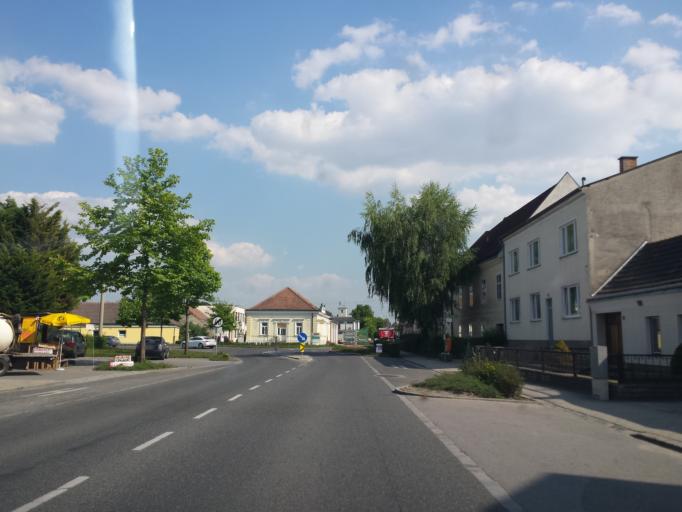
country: AT
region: Lower Austria
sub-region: Politischer Bezirk Ganserndorf
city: Markgrafneusiedl
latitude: 48.2677
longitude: 16.6311
